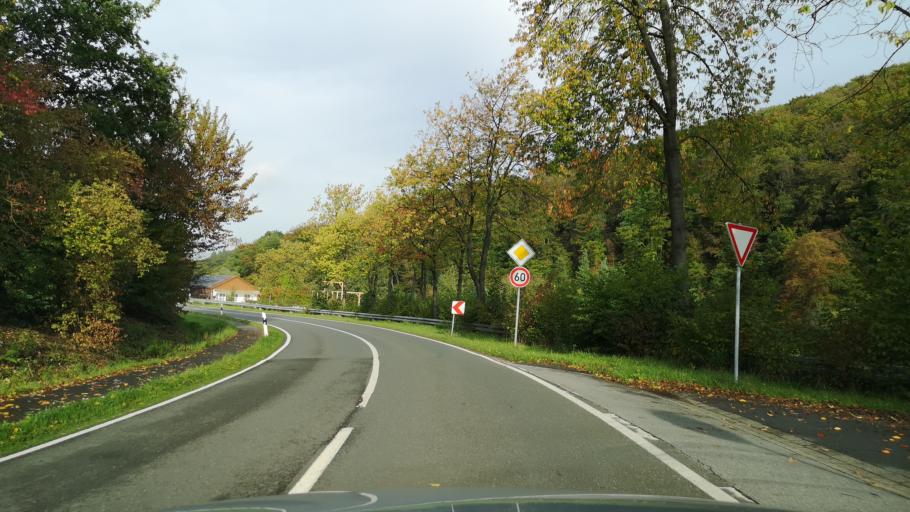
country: DE
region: North Rhine-Westphalia
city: Hattingen
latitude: 51.3573
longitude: 7.1689
